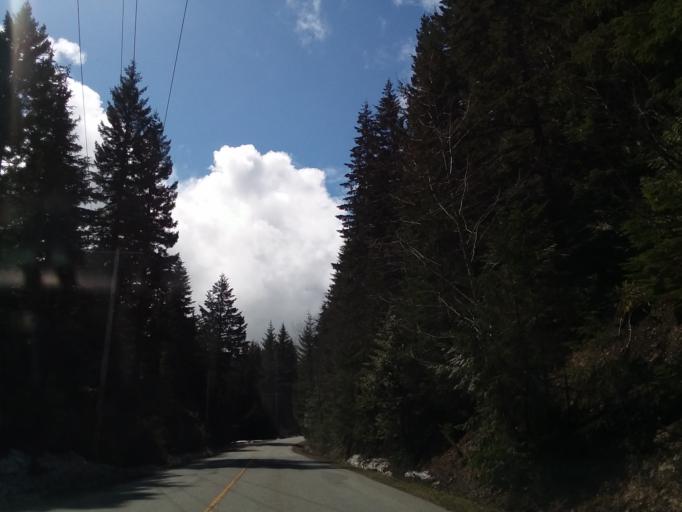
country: CA
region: British Columbia
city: Whistler
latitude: 50.1080
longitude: -122.9898
